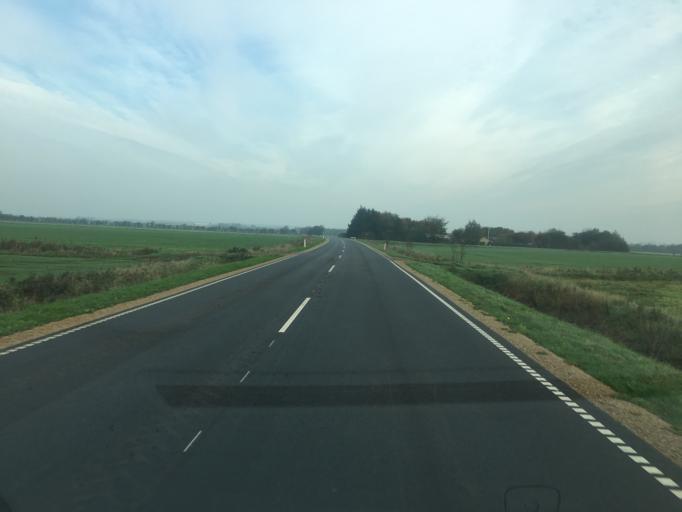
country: DK
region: South Denmark
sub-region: Tonder Kommune
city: Logumkloster
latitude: 55.1001
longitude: 9.0277
